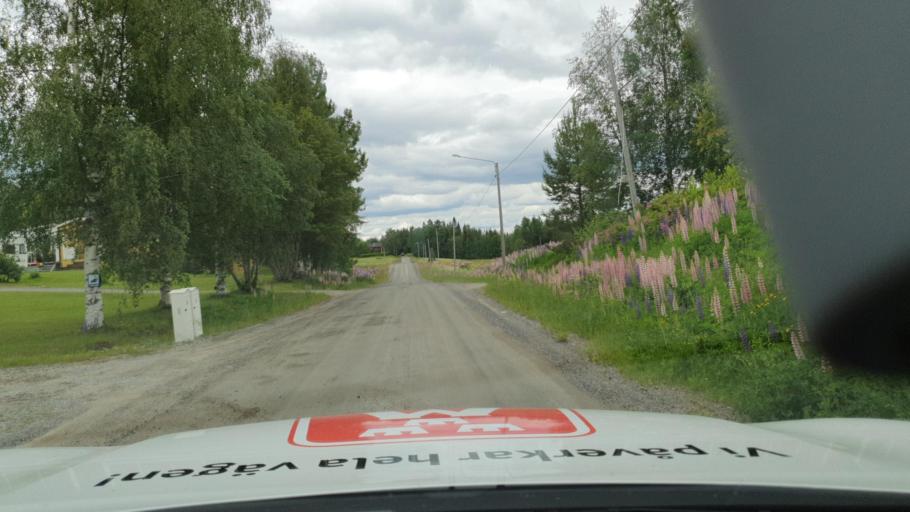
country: SE
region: Vaesterbotten
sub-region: Bjurholms Kommun
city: Bjurholm
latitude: 63.7372
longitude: 19.2902
